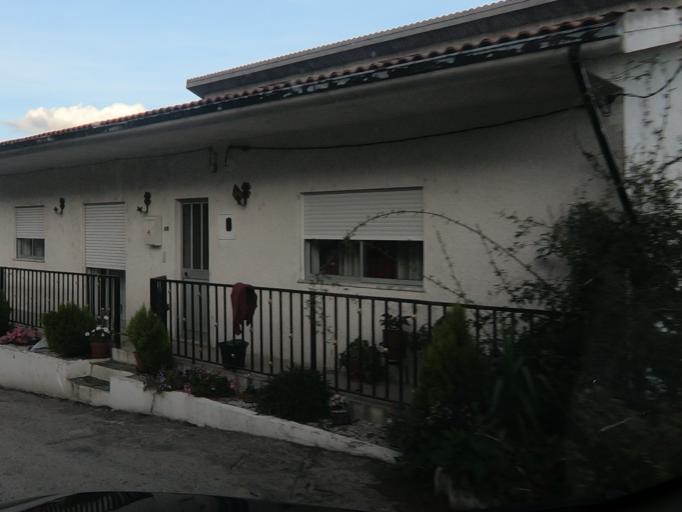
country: PT
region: Vila Real
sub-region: Santa Marta de Penaguiao
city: Santa Marta de Penaguiao
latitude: 41.2453
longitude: -7.8439
